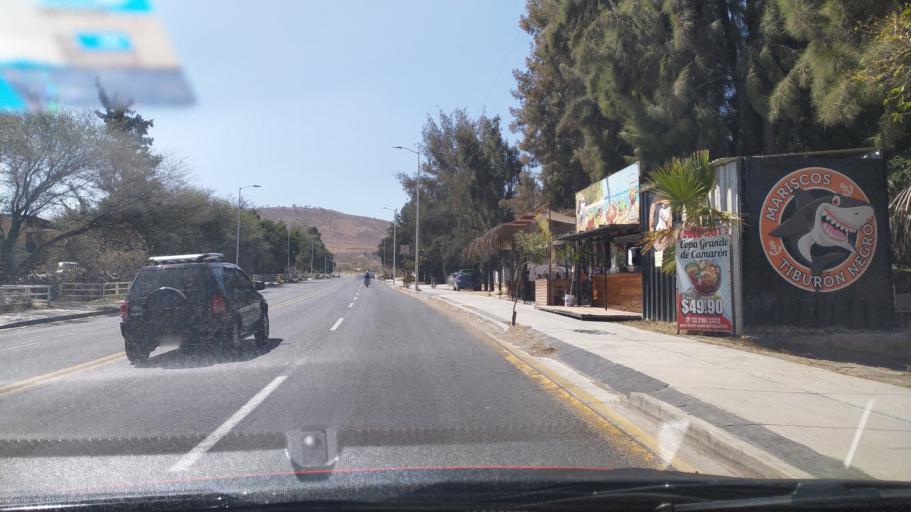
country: MX
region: Jalisco
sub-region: Tlajomulco de Zuniga
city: Lomas del Sur
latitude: 20.4976
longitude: -103.4171
